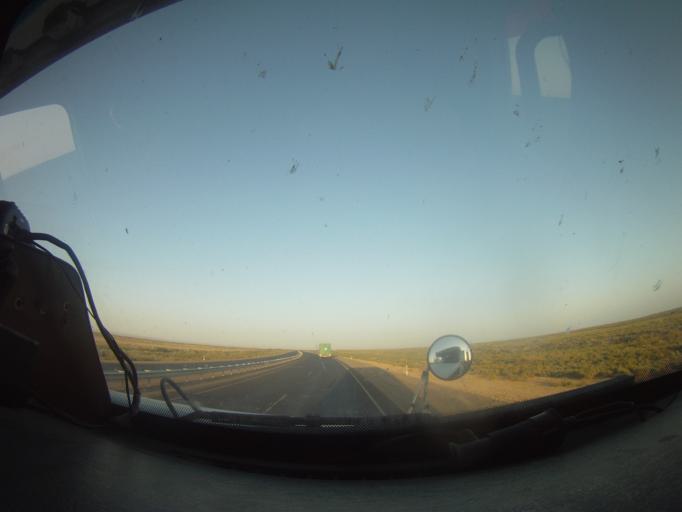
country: KZ
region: Qyzylorda
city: Shieli
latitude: 44.1113
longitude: 67.0107
